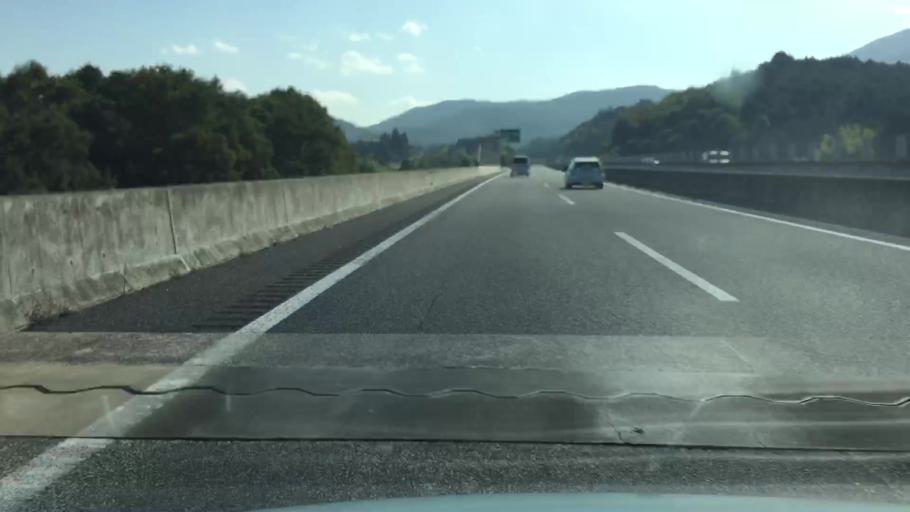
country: JP
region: Ibaraki
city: Iwase
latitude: 36.3474
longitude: 140.1693
